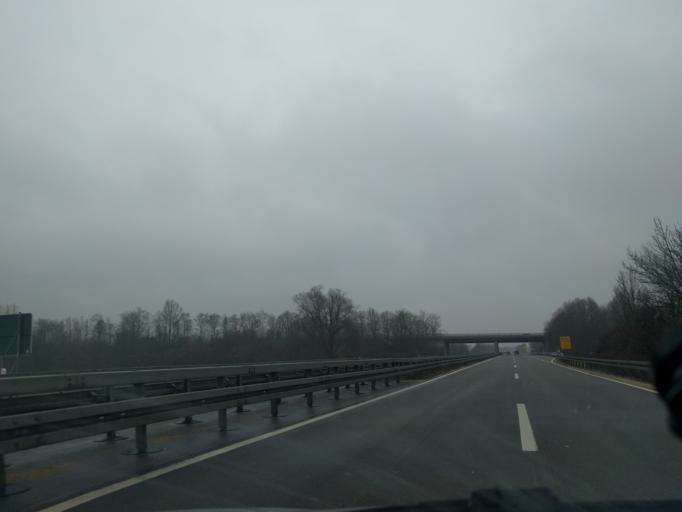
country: DE
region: Bavaria
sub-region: Swabia
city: Mertingen
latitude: 48.6580
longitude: 10.8312
